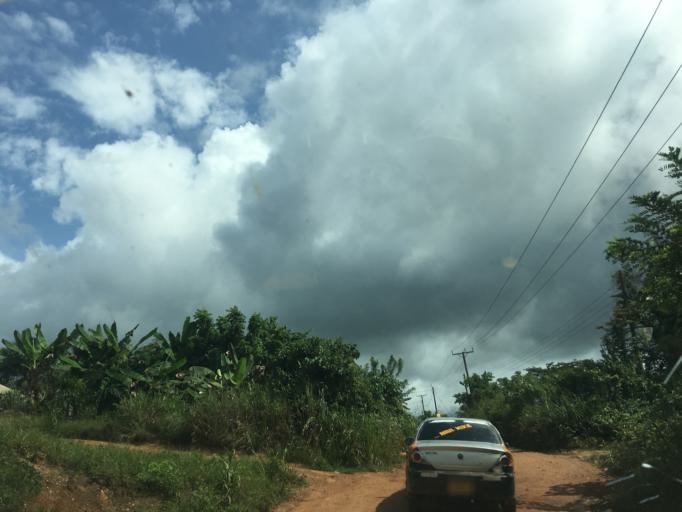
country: GH
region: Western
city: Wassa-Akropong
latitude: 5.7920
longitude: -2.4288
